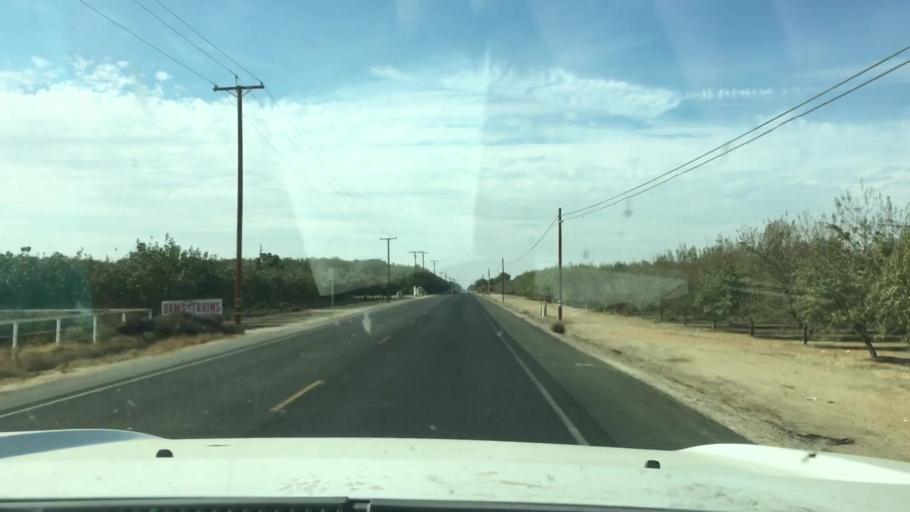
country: US
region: California
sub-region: Kern County
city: Shafter
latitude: 35.4999
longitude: -119.3024
